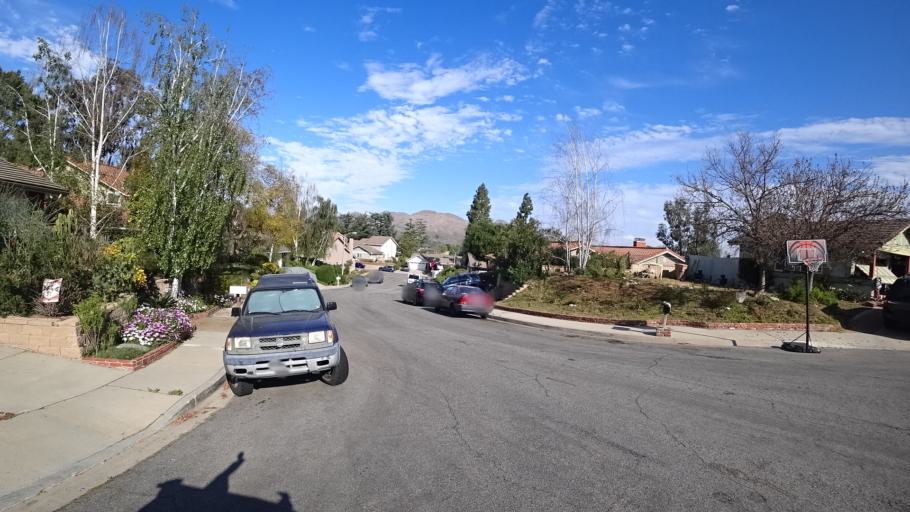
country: US
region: California
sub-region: Ventura County
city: Casa Conejo
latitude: 34.1713
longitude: -118.9474
